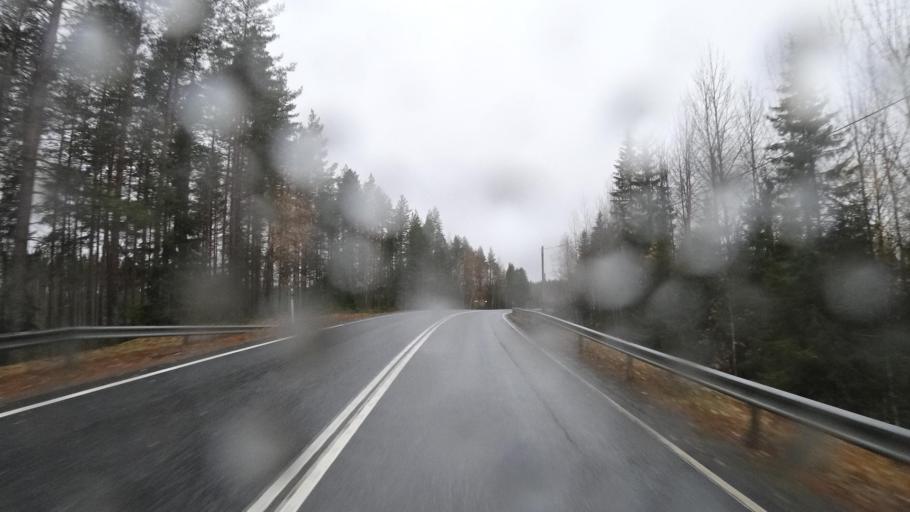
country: FI
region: Northern Savo
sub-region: Koillis-Savo
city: Tuusniemi
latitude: 62.8681
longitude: 28.4057
